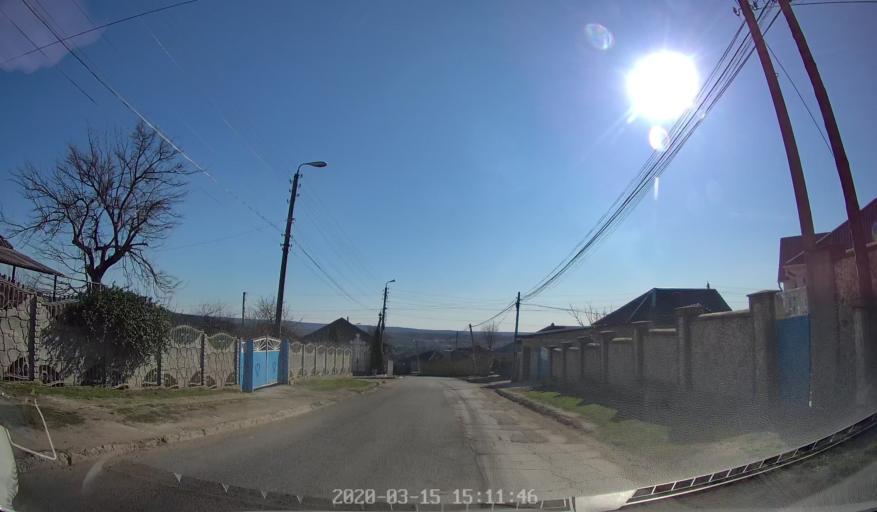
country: MD
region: Orhei
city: Orhei
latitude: 47.2608
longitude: 28.7752
